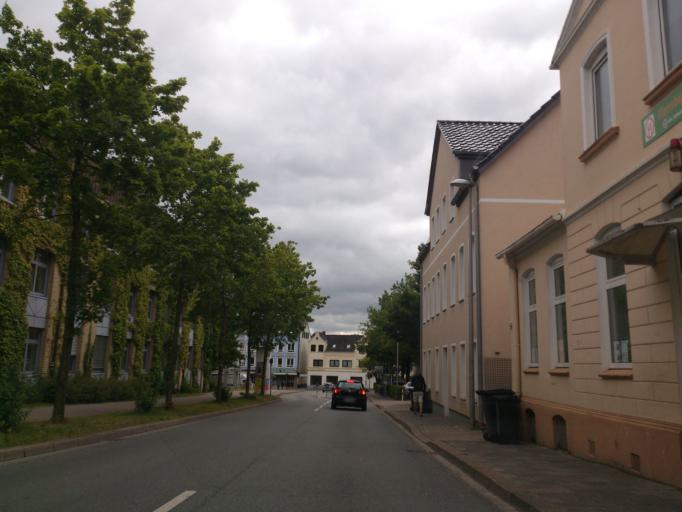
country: DE
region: Schleswig-Holstein
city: Flensburg
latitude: 54.7929
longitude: 9.4230
